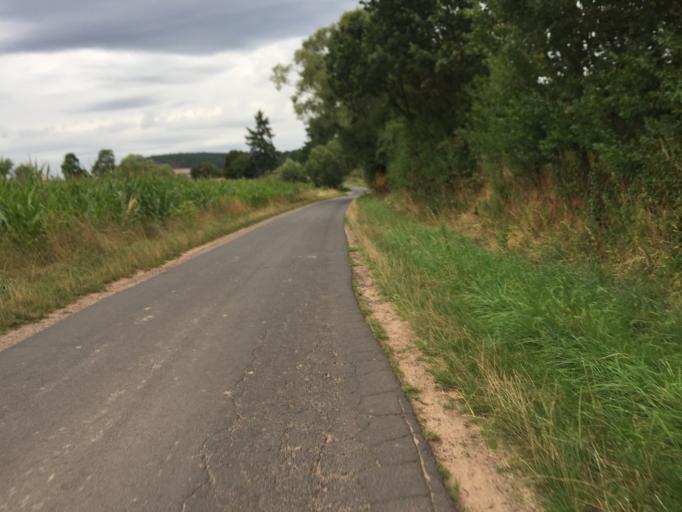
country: DE
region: Hesse
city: Breitenbach
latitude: 50.9239
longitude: 9.7891
